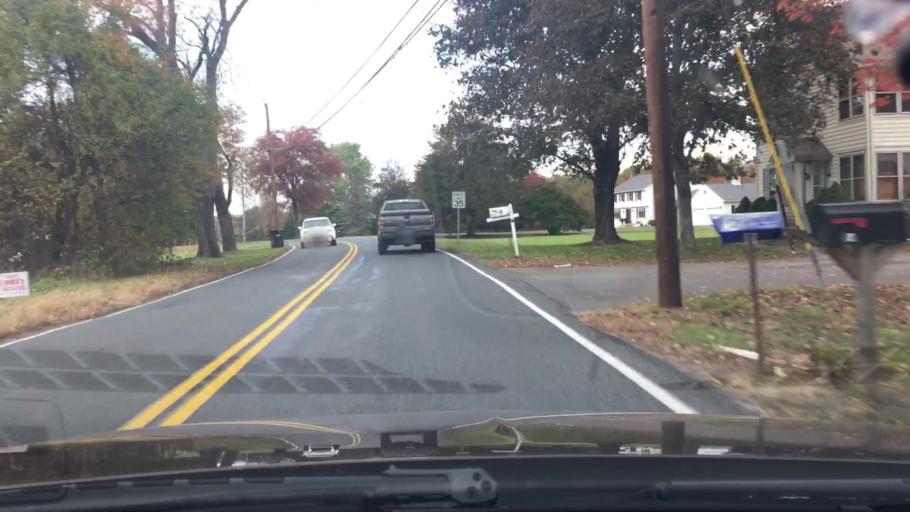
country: US
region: Connecticut
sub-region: Tolland County
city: Somers
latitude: 41.9874
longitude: -72.4913
